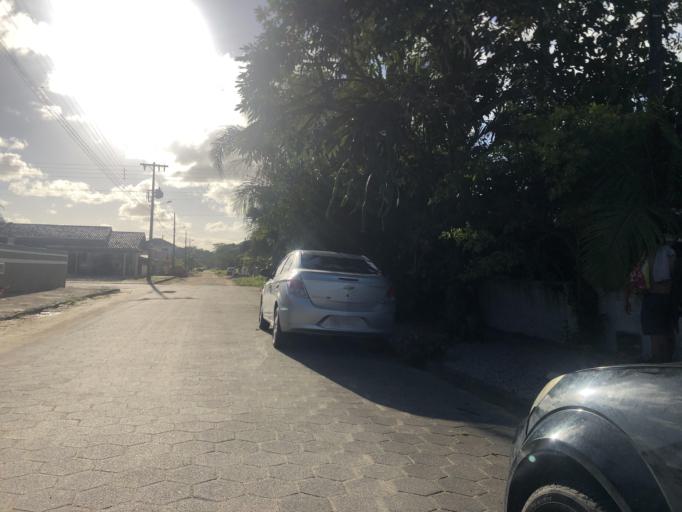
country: BR
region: Santa Catarina
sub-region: Sao Francisco Do Sul
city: Sao Francisco do Sul
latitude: -26.2171
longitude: -48.5330
